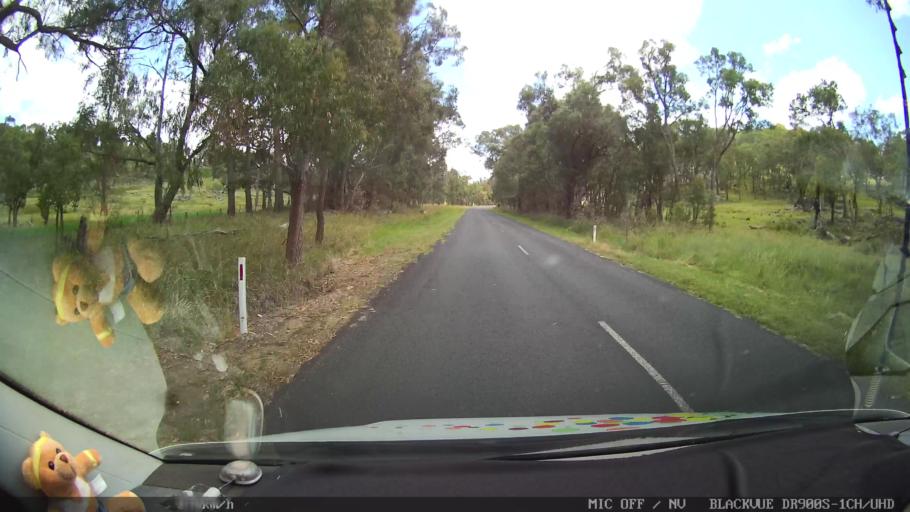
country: AU
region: New South Wales
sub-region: Glen Innes Severn
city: Glen Innes
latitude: -29.4918
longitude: 151.6823
